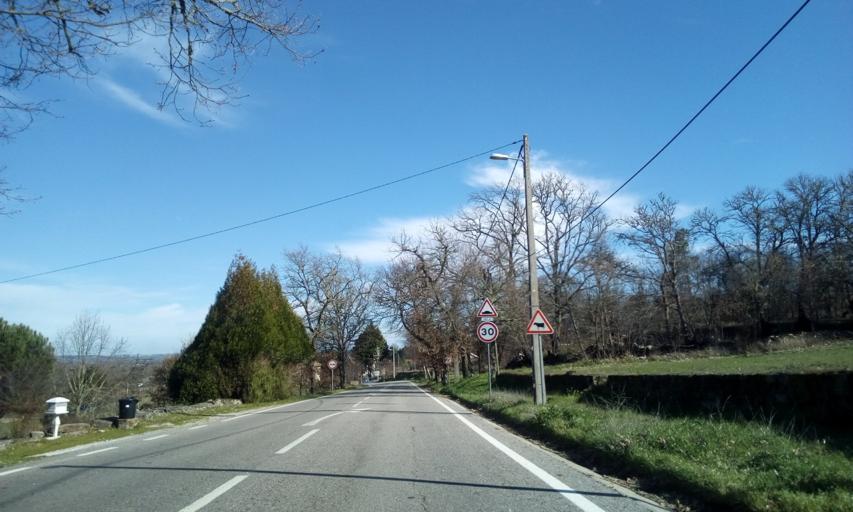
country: PT
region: Guarda
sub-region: Guarda
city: Sequeira
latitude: 40.5963
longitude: -7.1284
